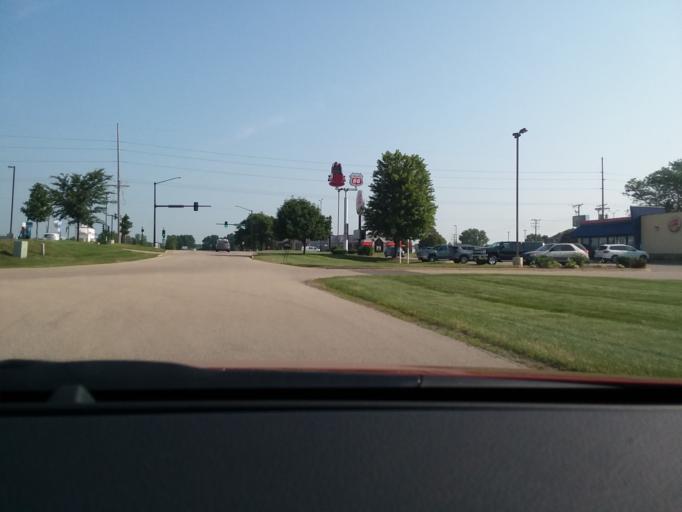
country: US
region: Wisconsin
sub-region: Dane County
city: De Forest
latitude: 43.2493
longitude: -89.3734
